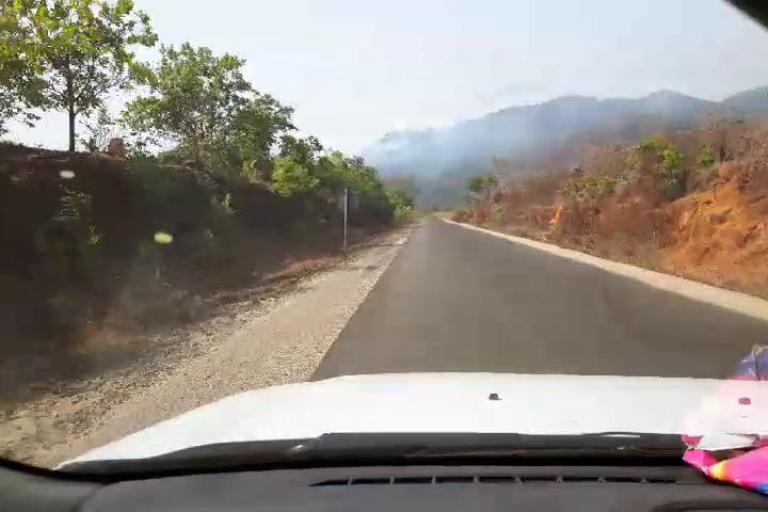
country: SL
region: Western Area
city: Waterloo
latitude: 8.2501
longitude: -13.1535
